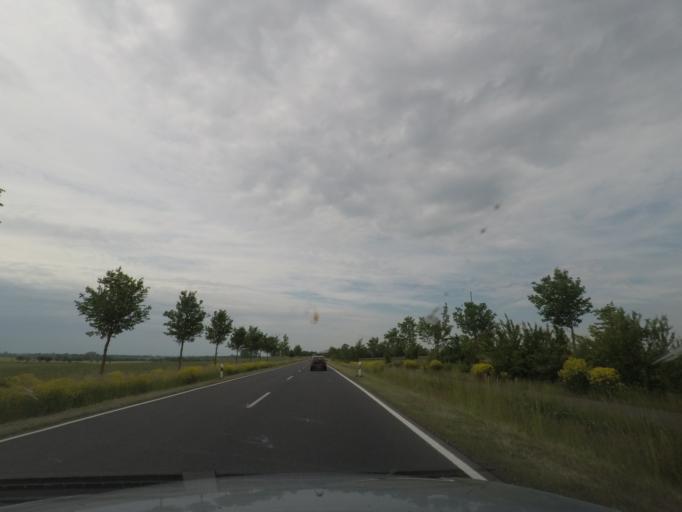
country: DE
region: Brandenburg
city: Prenzlau
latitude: 53.3343
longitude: 13.9004
